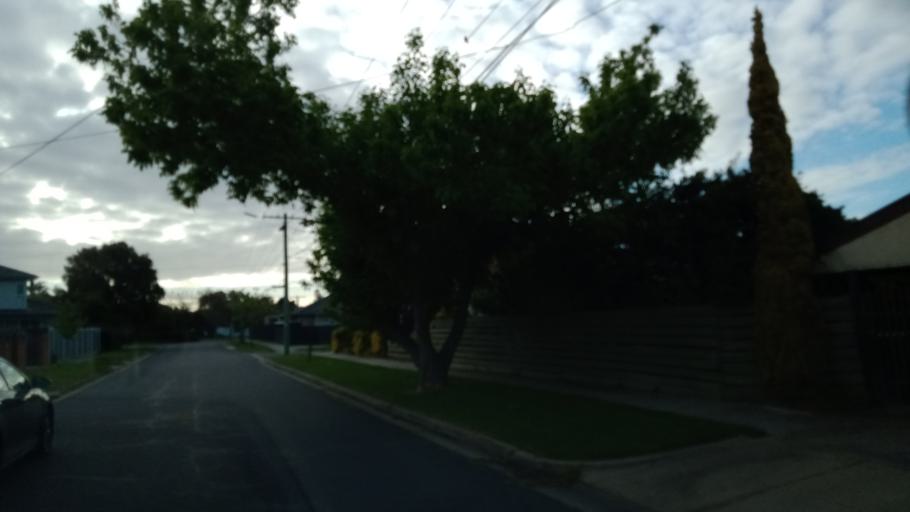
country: AU
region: Victoria
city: McKinnon
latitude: -37.9315
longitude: 145.0520
